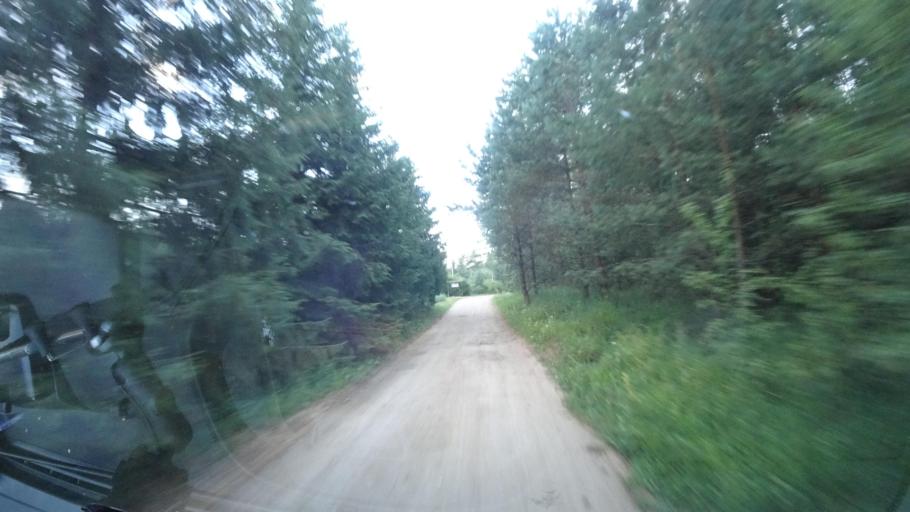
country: LT
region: Vilnius County
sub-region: Trakai
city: Rudiskes
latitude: 54.5082
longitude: 24.8895
